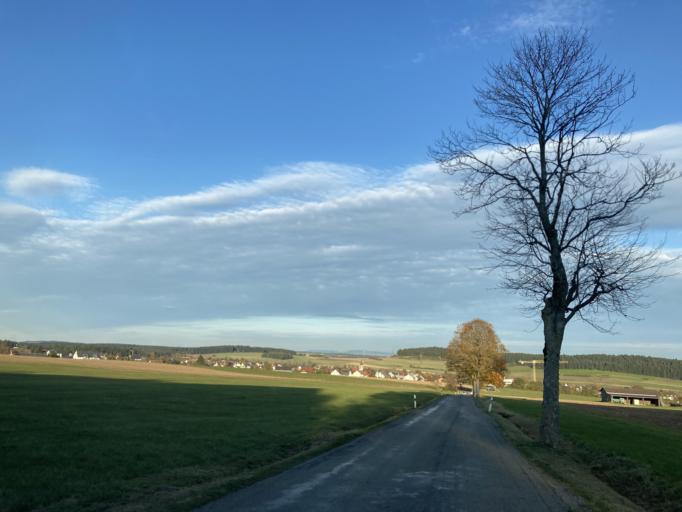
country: DE
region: Baden-Wuerttemberg
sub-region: Freiburg Region
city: Braunlingen
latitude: 47.9942
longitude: 8.3962
